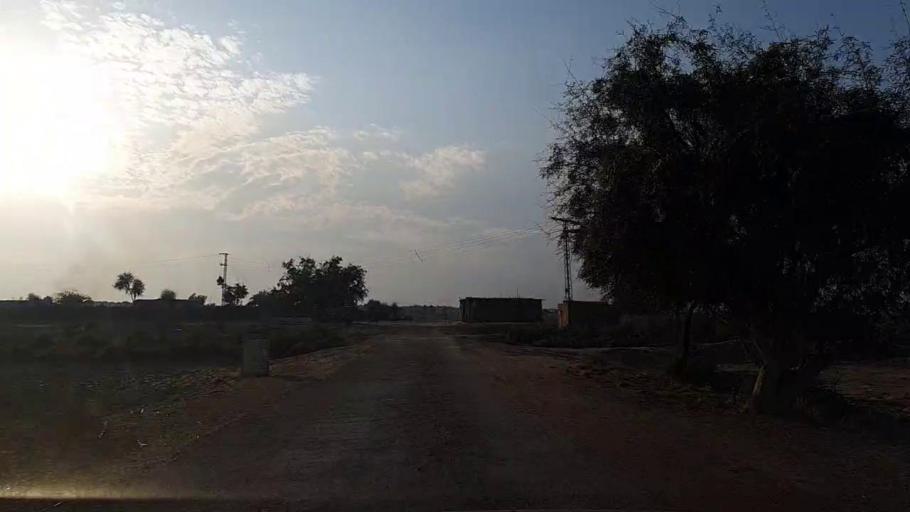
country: PK
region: Sindh
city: Jam Sahib
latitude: 26.3945
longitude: 68.5093
